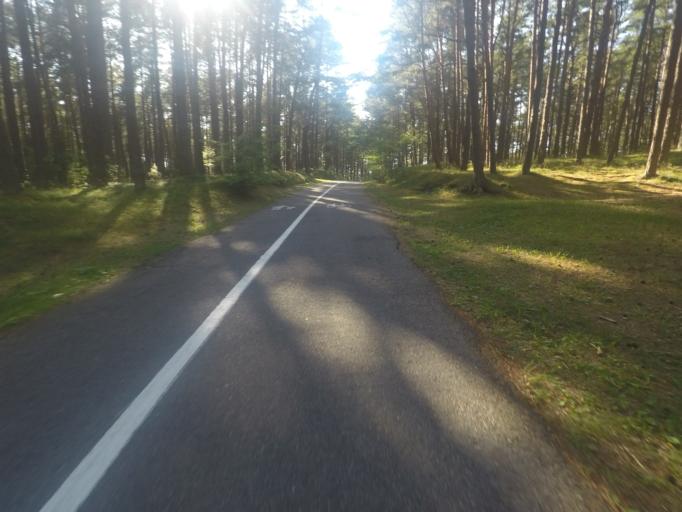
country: LT
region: Klaipedos apskritis
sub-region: Klaipeda
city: Klaipeda
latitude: 55.5462
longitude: 21.1130
